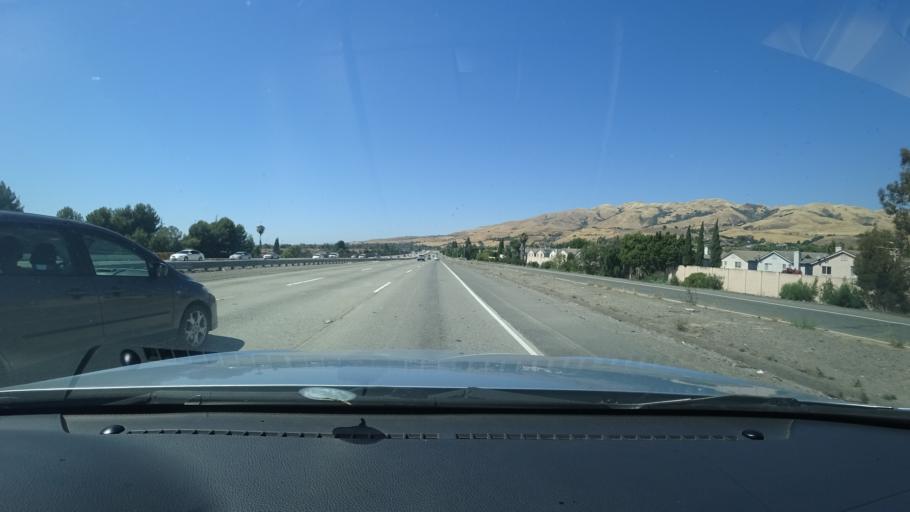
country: US
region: California
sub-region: Santa Clara County
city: Milpitas
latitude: 37.4364
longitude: -121.8888
